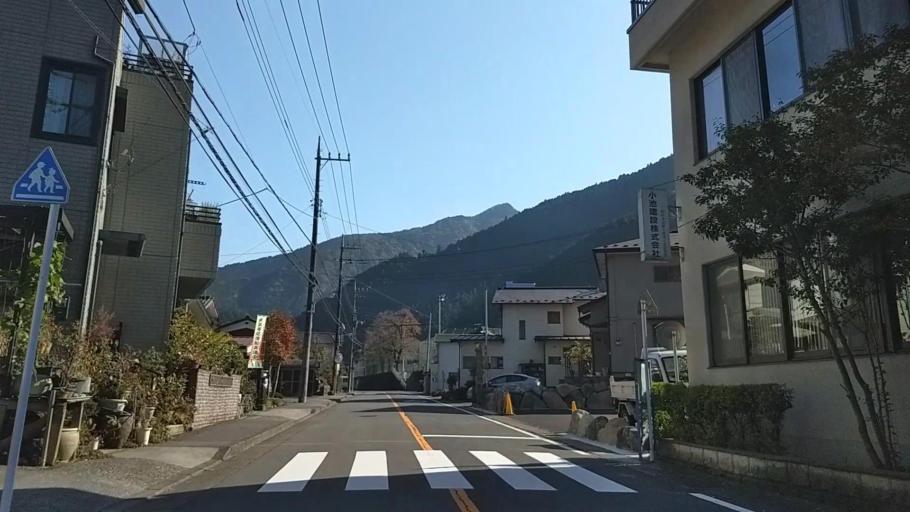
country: JP
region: Tokyo
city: Itsukaichi
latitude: 35.8056
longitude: 139.1002
